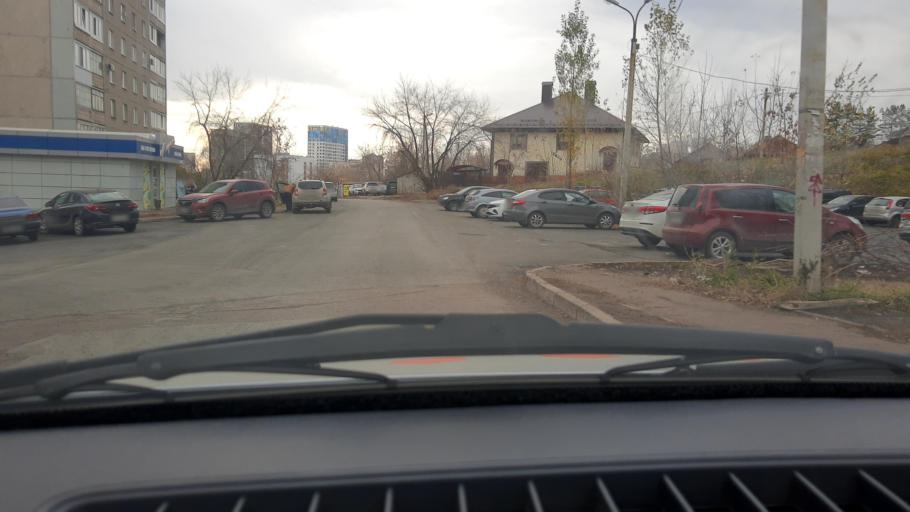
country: RU
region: Bashkortostan
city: Ufa
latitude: 54.7866
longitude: 56.0446
